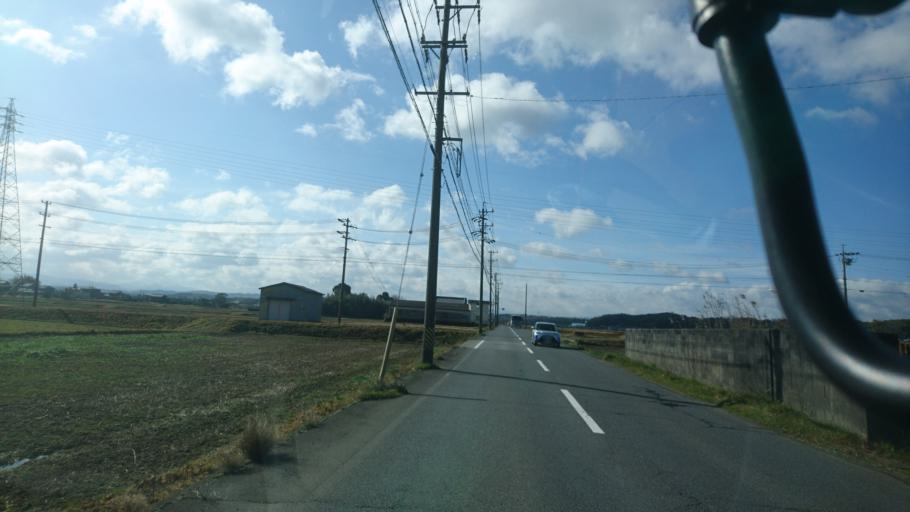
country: JP
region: Mie
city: Ueno-ebisumachi
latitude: 34.7523
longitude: 136.1108
